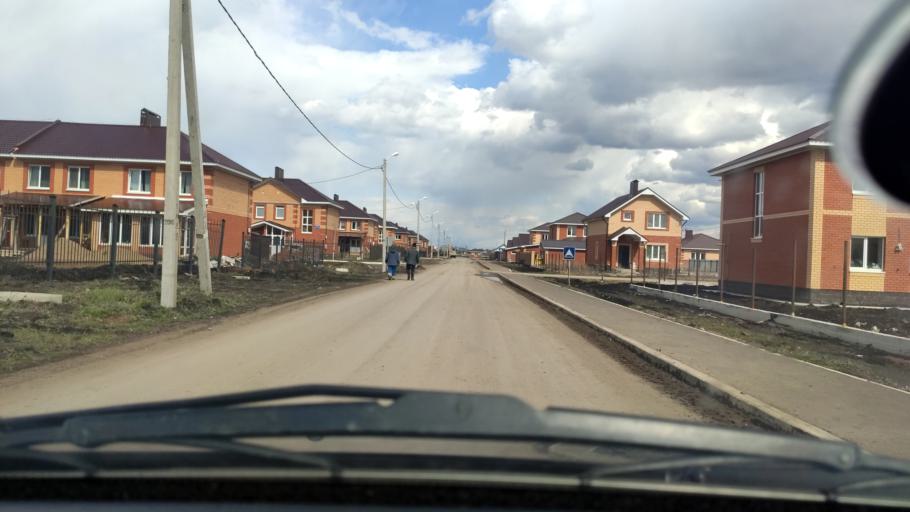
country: RU
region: Bashkortostan
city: Ufa
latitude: 54.6197
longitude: 55.8837
